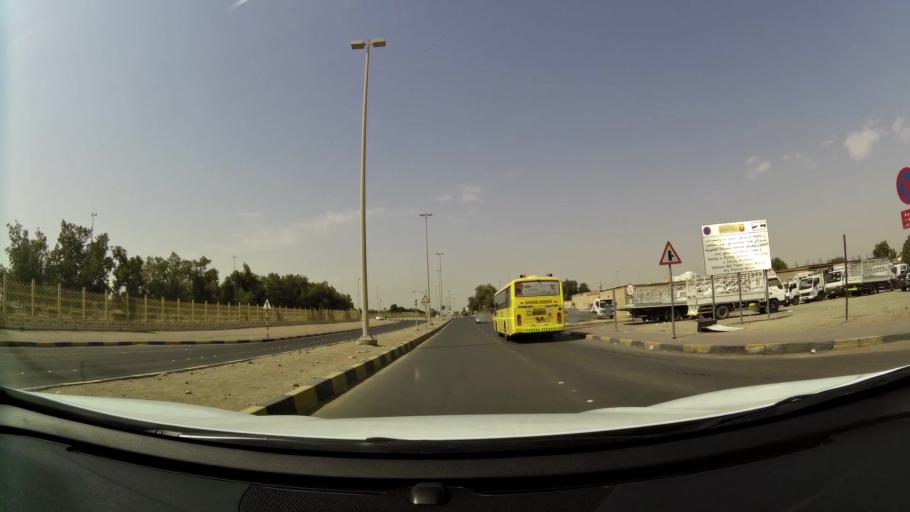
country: AE
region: Abu Dhabi
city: Abu Dhabi
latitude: 24.2882
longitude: 54.6397
